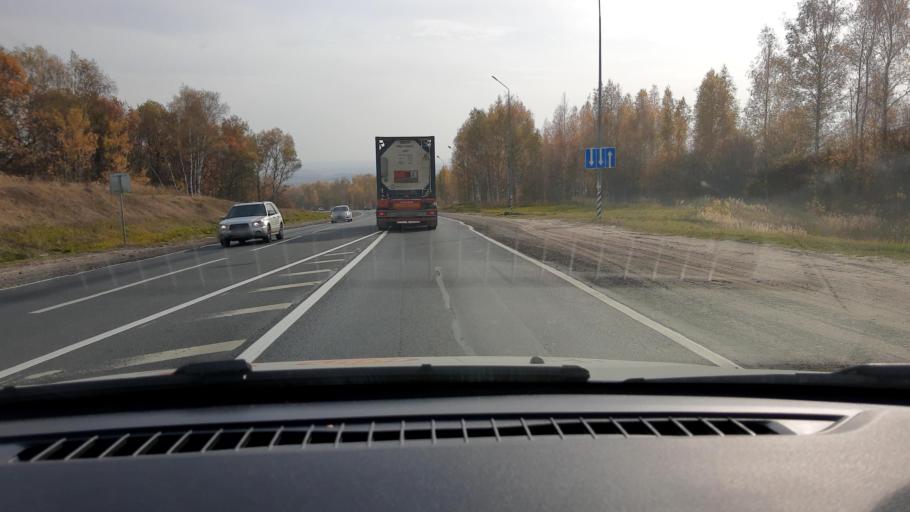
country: RU
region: Nizjnij Novgorod
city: Kstovo
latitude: 56.1079
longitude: 44.2869
